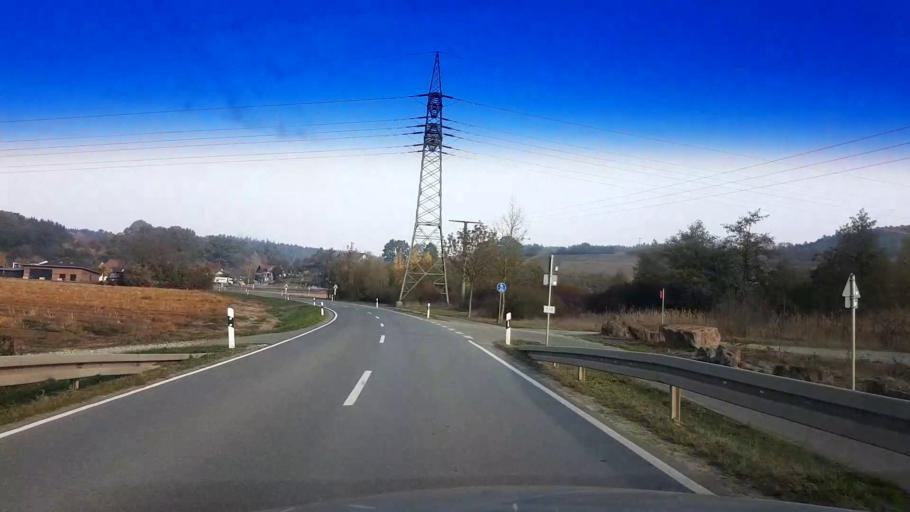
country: DE
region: Bavaria
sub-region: Upper Franconia
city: Altenkunstadt
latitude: 50.1220
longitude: 11.3002
